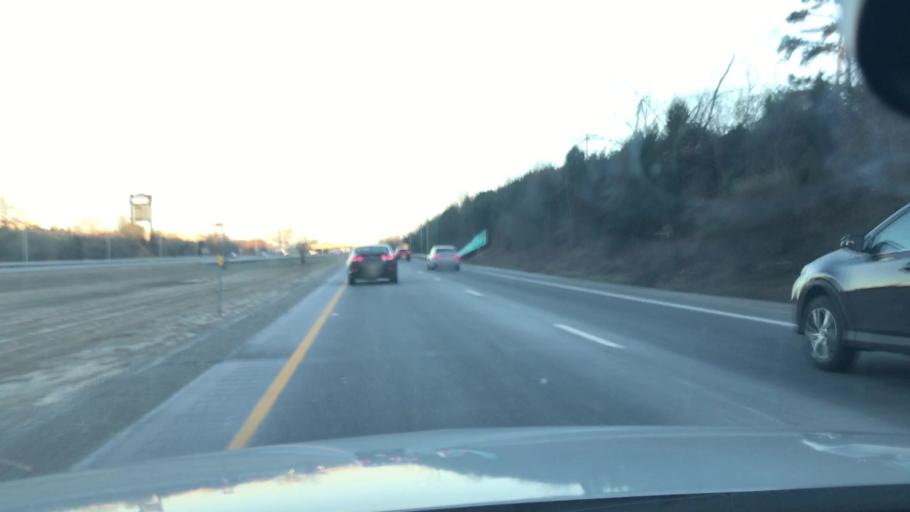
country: US
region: New Jersey
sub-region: Camden County
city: Sicklerville
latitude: 39.7379
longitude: -75.0134
